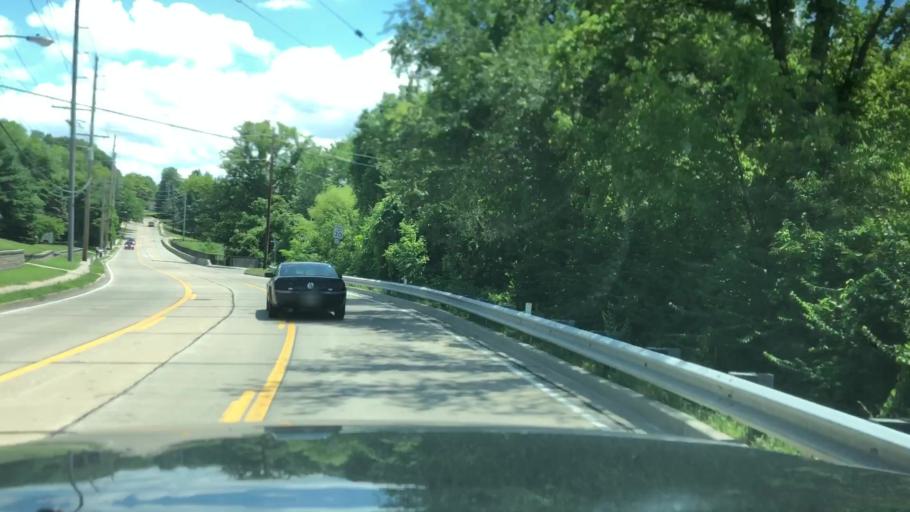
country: US
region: Missouri
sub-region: Saint Charles County
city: Saint Charles
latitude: 38.8099
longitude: -90.5127
